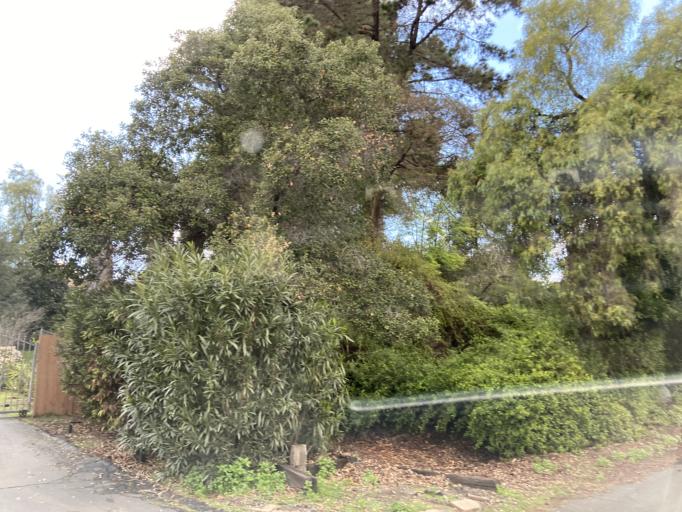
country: US
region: California
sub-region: San Diego County
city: Casa de Oro-Mount Helix
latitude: 32.7673
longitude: -116.9657
